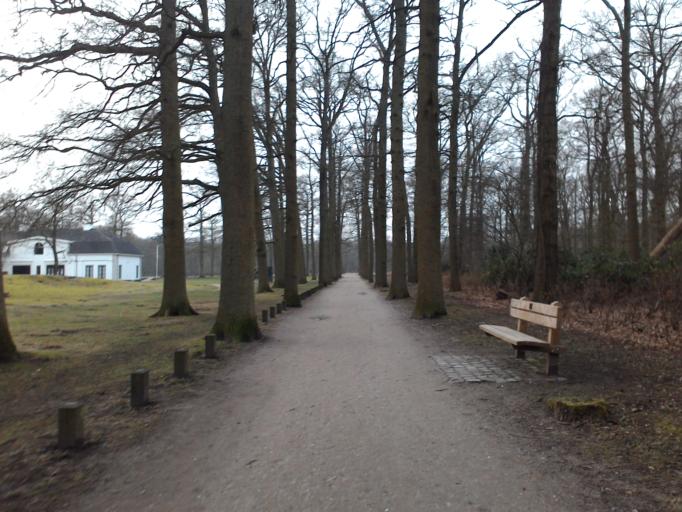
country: NL
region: Utrecht
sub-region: Gemeente De Bilt
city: De Bilt
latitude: 52.1062
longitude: 5.2024
